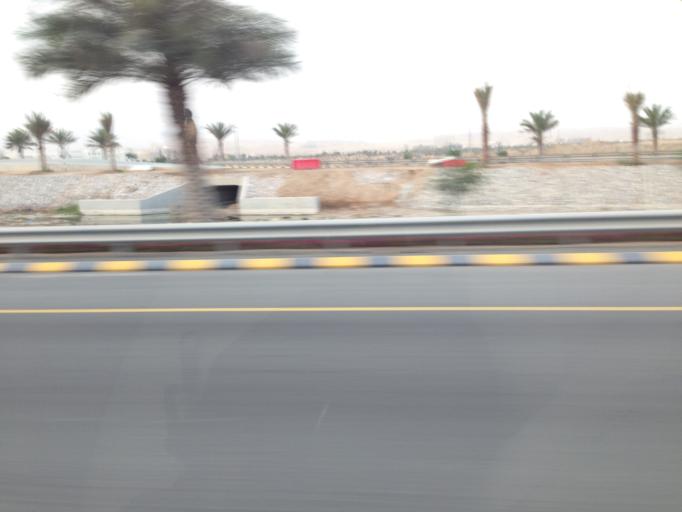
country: OM
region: Muhafazat Masqat
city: Bawshar
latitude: 23.6011
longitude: 58.3258
